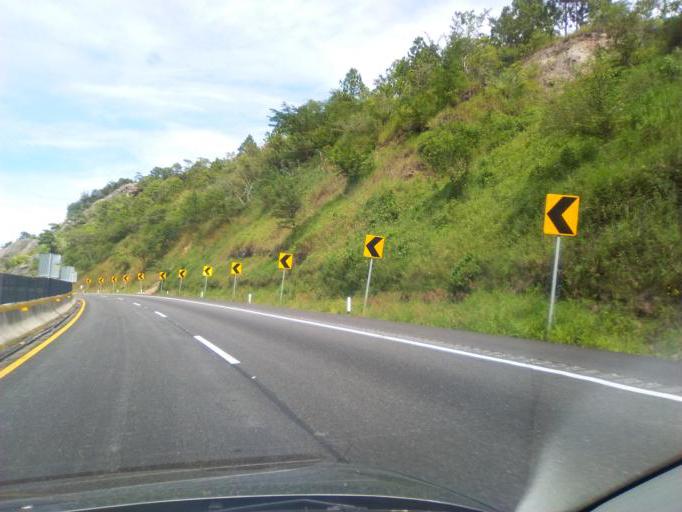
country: MX
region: Guerrero
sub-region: Chilpancingo de los Bravo
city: Acahuizotla
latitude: 17.3220
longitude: -99.4756
